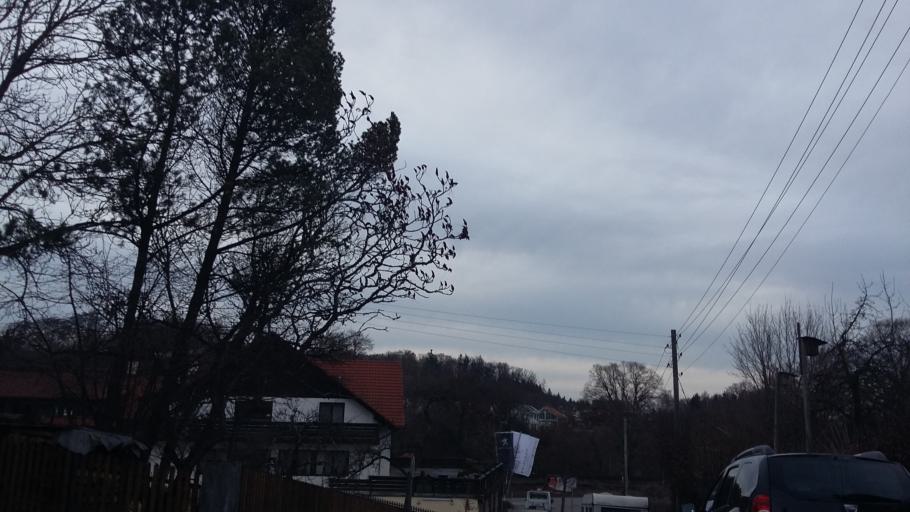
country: DE
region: Bavaria
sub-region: Upper Bavaria
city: Wessling
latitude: 48.0779
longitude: 11.2583
